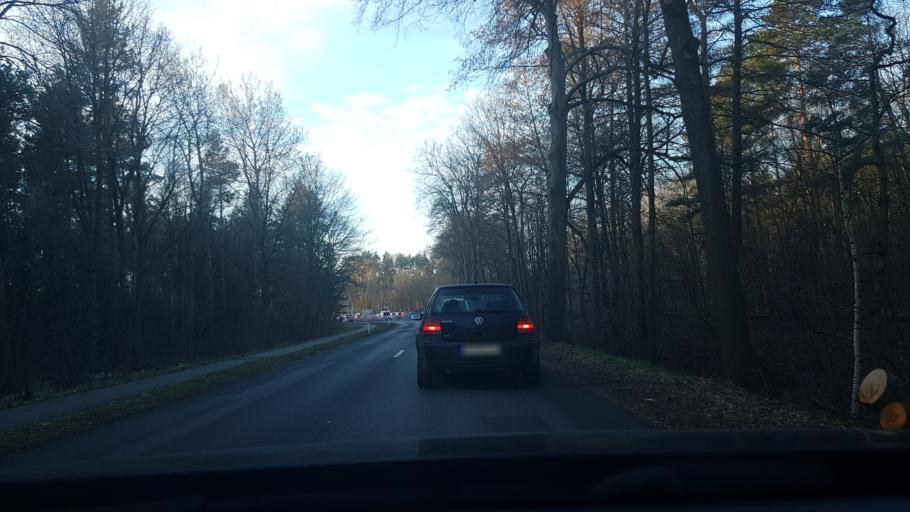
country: DE
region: Lower Saxony
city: Gifhorn
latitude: 52.4986
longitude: 10.5709
